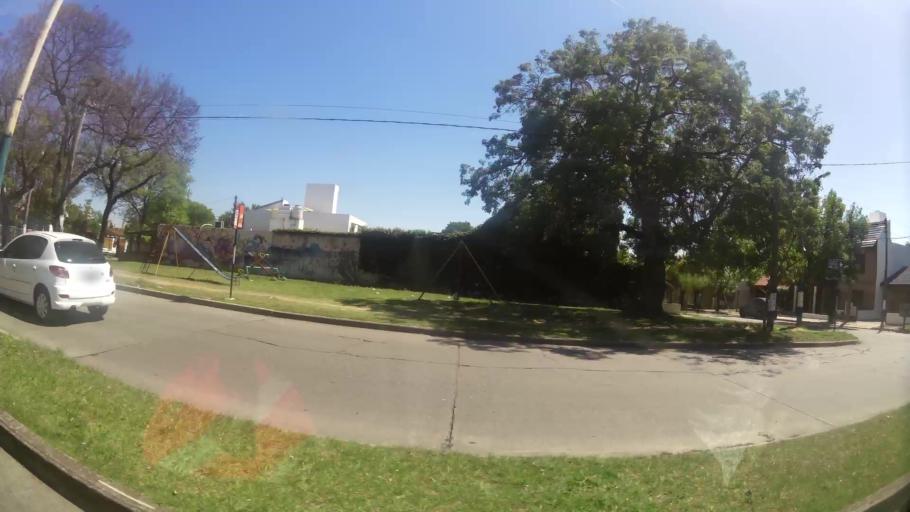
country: AR
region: Cordoba
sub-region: Departamento de Capital
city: Cordoba
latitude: -31.4202
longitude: -64.2149
